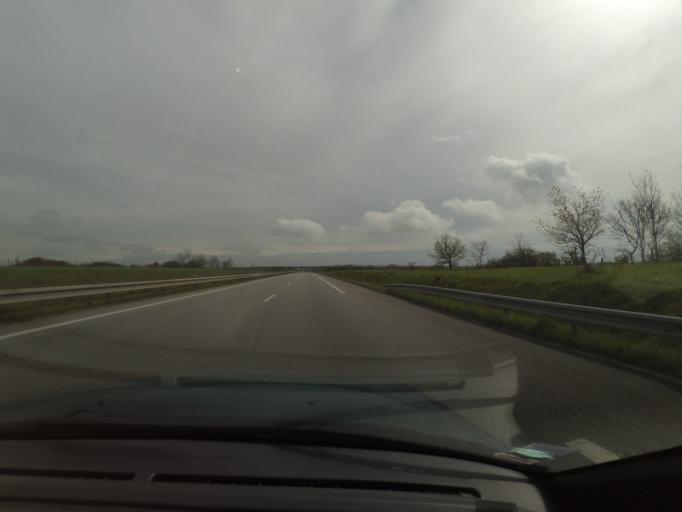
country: FR
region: Pays de la Loire
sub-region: Departement de la Loire-Atlantique
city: Ancenis
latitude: 47.4050
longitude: -1.1787
